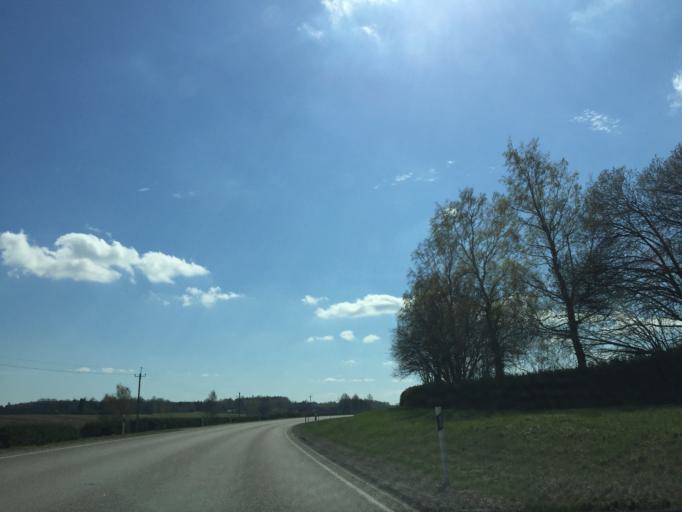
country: EE
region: Valgamaa
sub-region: Torva linn
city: Torva
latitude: 58.0465
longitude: 26.1928
